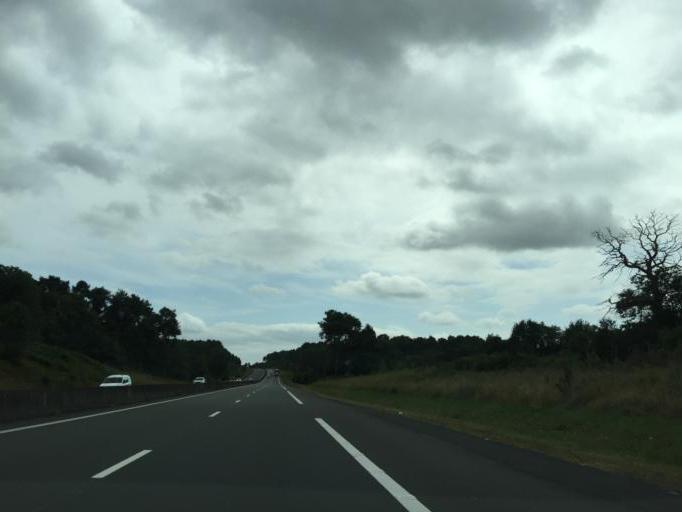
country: FR
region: Pays de la Loire
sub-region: Departement de la Sarthe
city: Mayet
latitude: 47.7594
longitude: 0.3144
